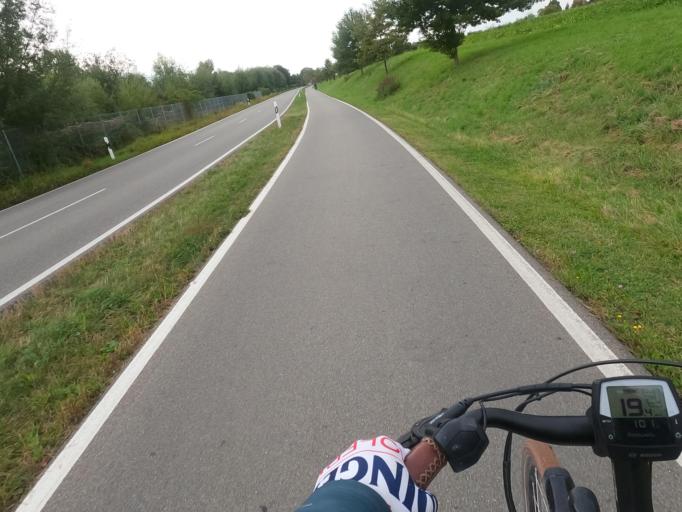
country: CH
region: Thurgau
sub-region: Kreuzlingen District
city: Gottlieben
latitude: 47.6909
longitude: 9.1224
